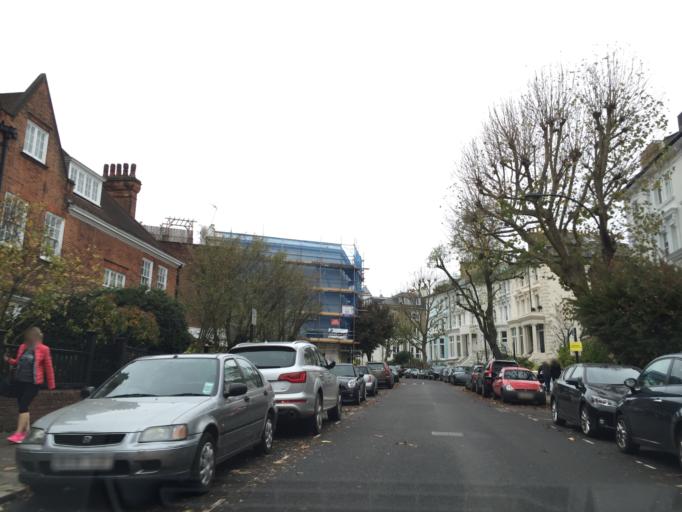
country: GB
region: England
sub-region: Greater London
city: Belsize Park
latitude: 51.5462
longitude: -0.1637
